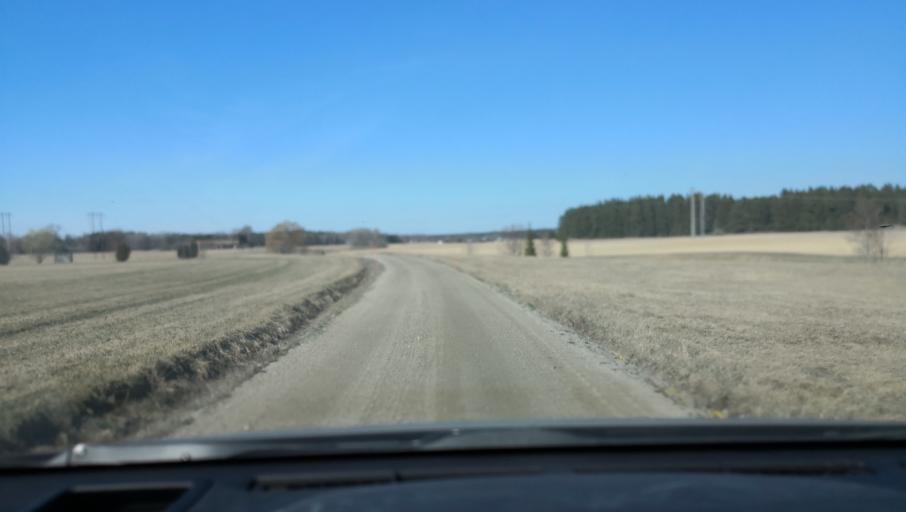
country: SE
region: Vaestmanland
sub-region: Sala Kommun
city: Sala
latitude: 59.8942
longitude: 16.5307
